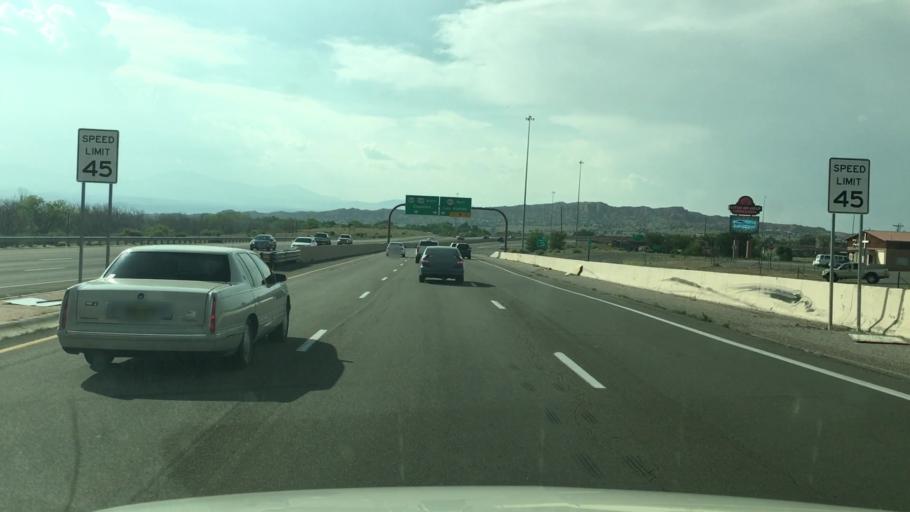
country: US
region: New Mexico
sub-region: Santa Fe County
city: Pojoaque
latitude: 35.8866
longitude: -106.0188
